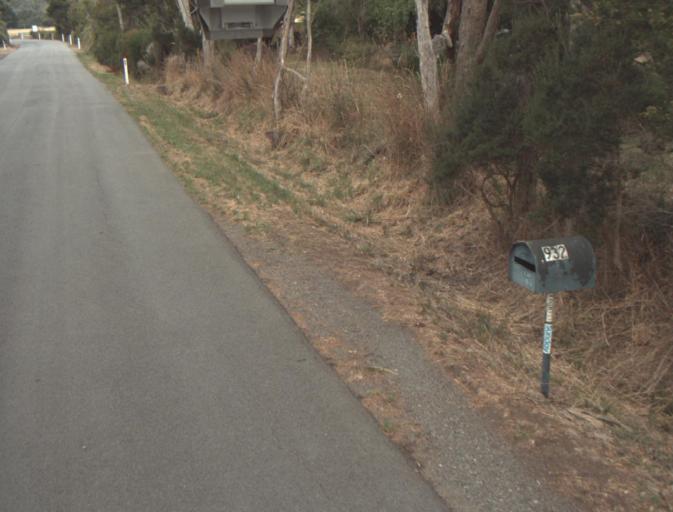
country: AU
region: Tasmania
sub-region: Launceston
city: Mayfield
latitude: -41.2848
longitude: 147.0019
